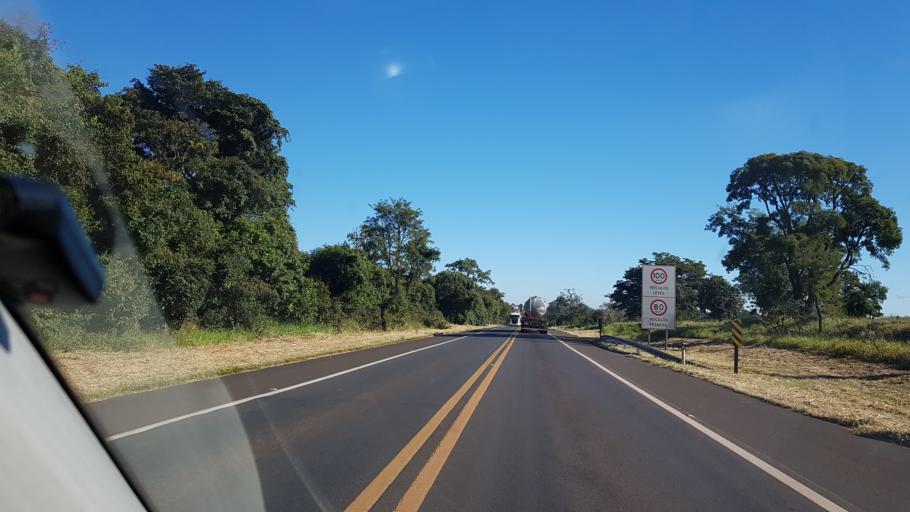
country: BR
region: Sao Paulo
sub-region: Assis
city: Assis
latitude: -22.5841
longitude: -50.5019
